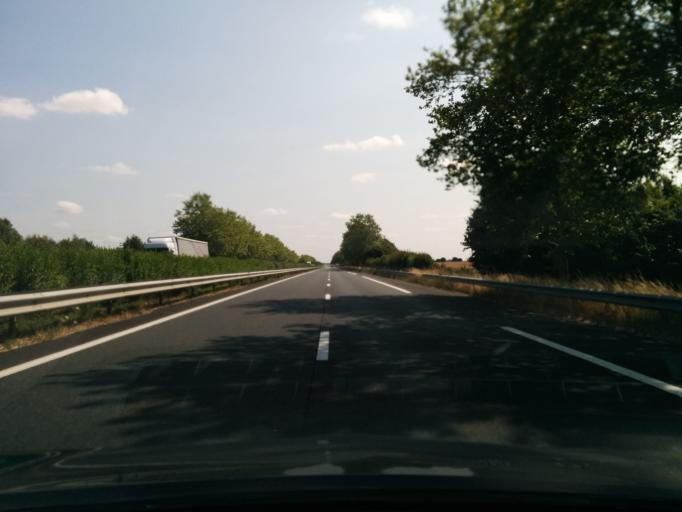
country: FR
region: Centre
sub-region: Departement de l'Indre
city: Montierchaume
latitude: 46.9149
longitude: 1.7393
